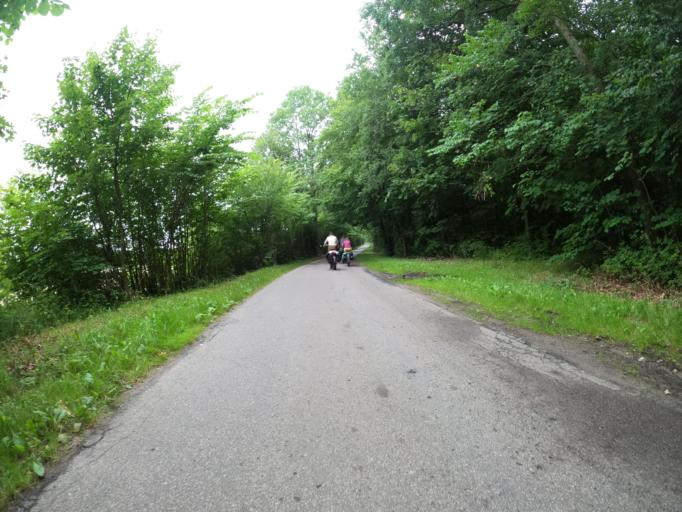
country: PL
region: West Pomeranian Voivodeship
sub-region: Powiat szczecinecki
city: Grzmiaca
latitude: 53.9372
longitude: 16.4543
